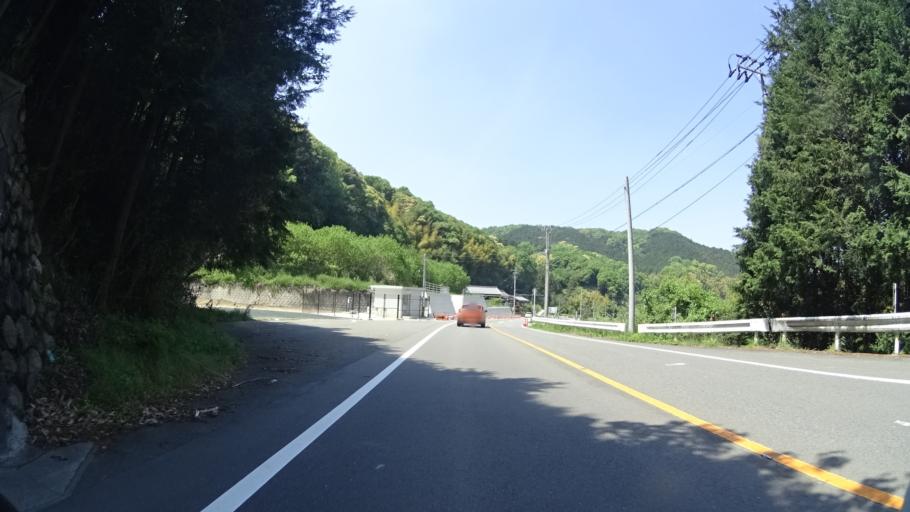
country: JP
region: Ehime
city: Hojo
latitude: 33.9848
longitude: 132.9082
